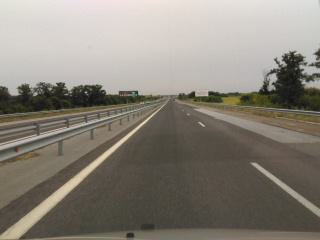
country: BG
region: Stara Zagora
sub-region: Obshtina Stara Zagora
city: Stara Zagora
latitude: 42.3224
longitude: 25.5879
